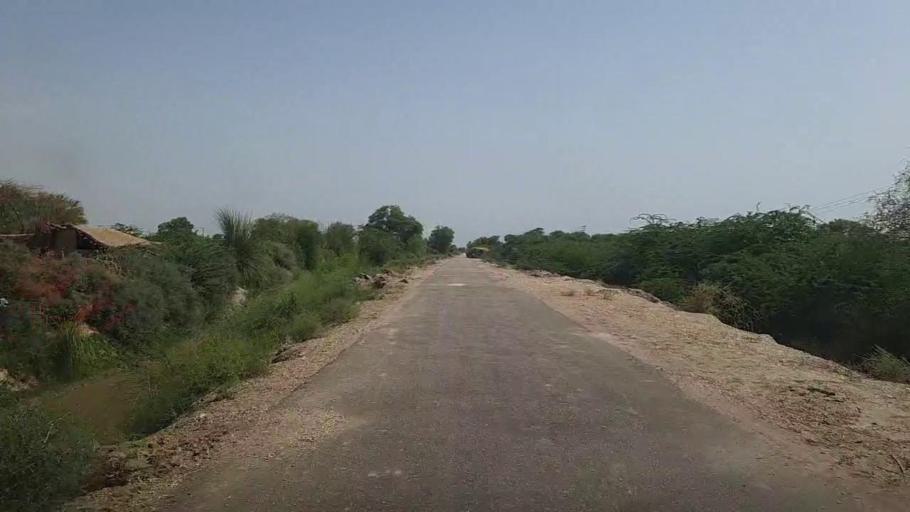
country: PK
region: Sindh
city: Pad Idan
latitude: 26.8215
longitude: 68.3278
